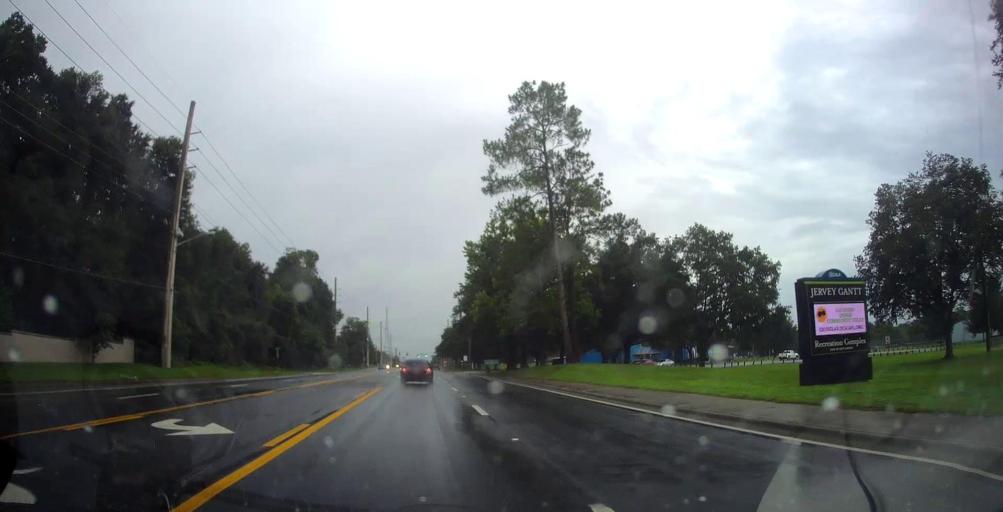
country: US
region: Florida
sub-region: Marion County
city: Ocala
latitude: 29.1668
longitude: -82.0869
